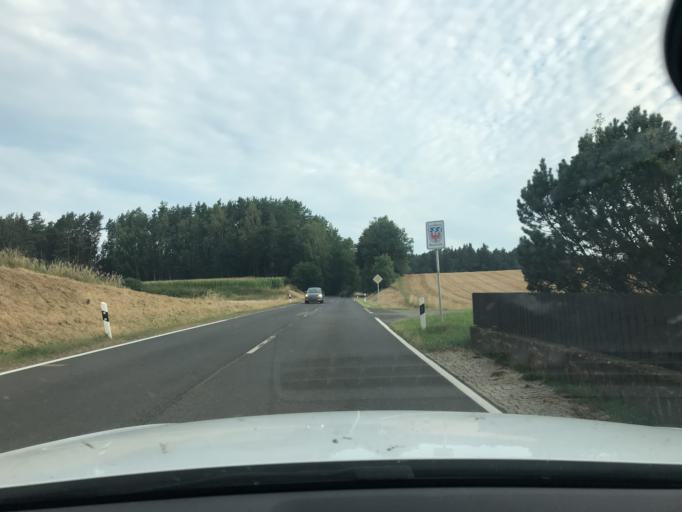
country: DE
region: Bavaria
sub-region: Upper Franconia
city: Pegnitz
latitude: 49.7560
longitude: 11.6060
